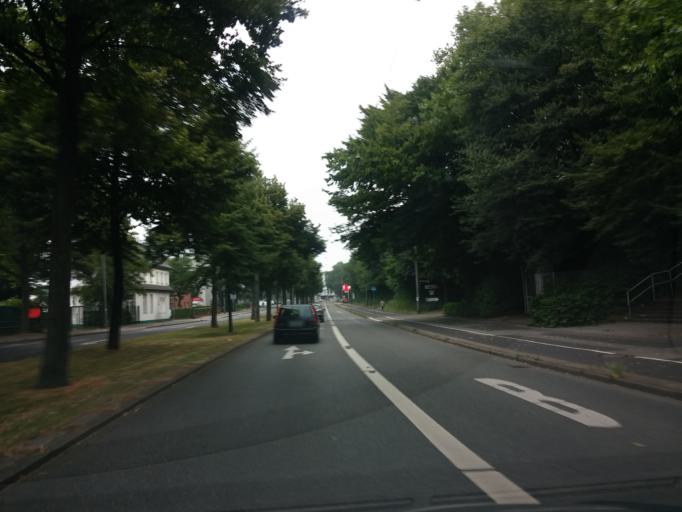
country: DE
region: North Rhine-Westphalia
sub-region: Regierungsbezirk Munster
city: Gladbeck
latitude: 51.5880
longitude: 7.0500
